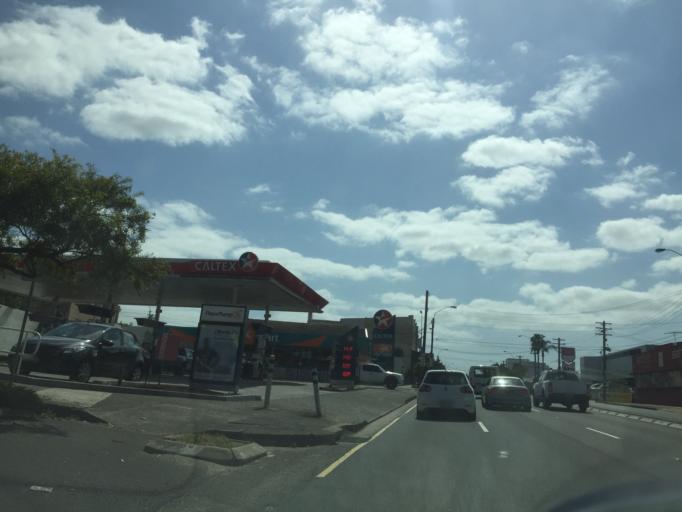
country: AU
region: New South Wales
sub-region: Rockdale
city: Arncliffe
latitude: -33.9257
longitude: 151.1595
